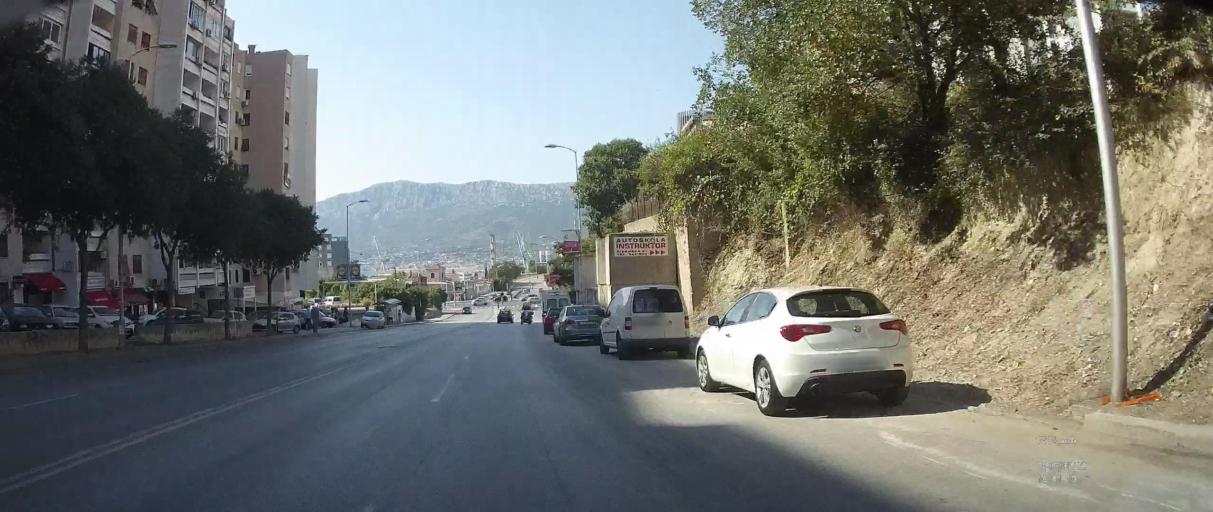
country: HR
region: Splitsko-Dalmatinska
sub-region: Grad Split
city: Split
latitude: 43.5181
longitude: 16.4503
